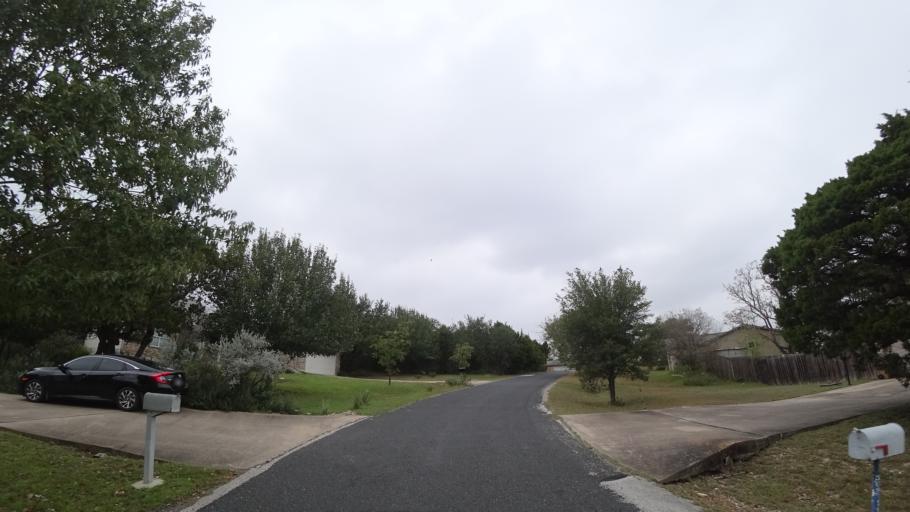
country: US
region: Texas
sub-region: Travis County
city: Barton Creek
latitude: 30.2408
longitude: -97.8902
